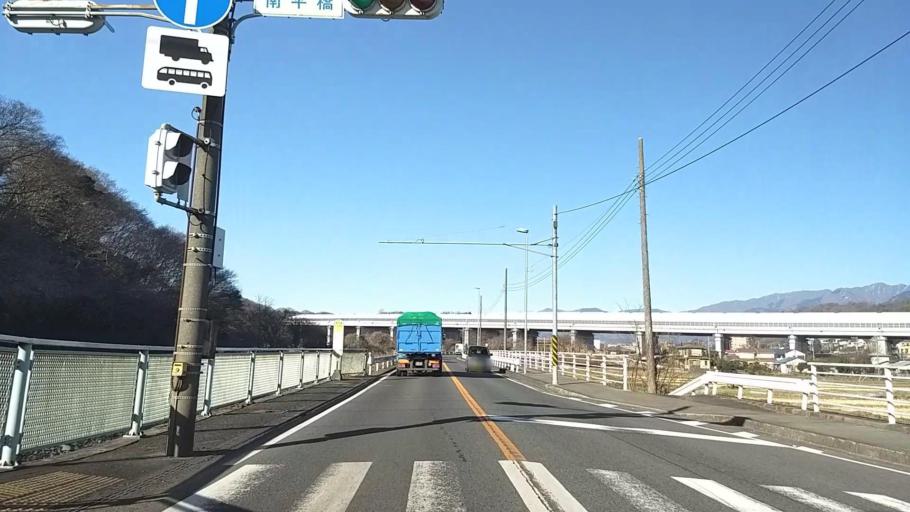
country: JP
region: Kanagawa
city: Hadano
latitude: 35.3581
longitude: 139.2535
